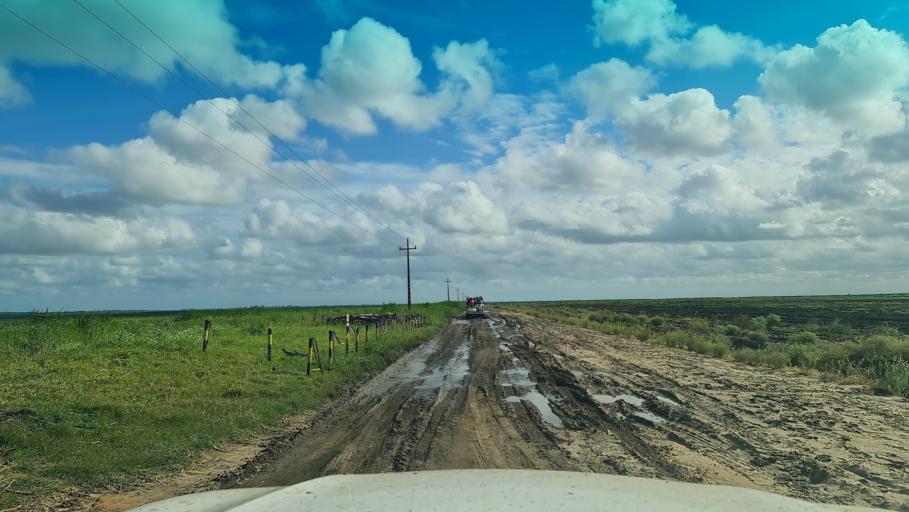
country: MZ
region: Maputo
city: Manhica
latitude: -25.4377
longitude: 32.8407
